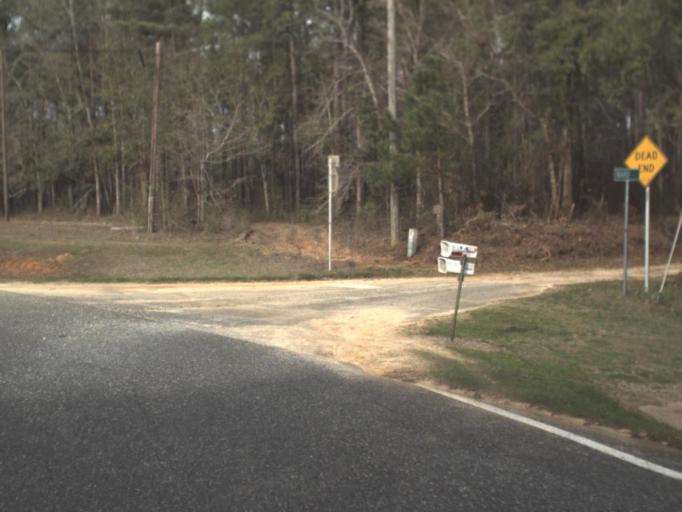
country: US
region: Florida
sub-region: Jefferson County
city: Monticello
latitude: 30.6315
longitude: -83.8729
